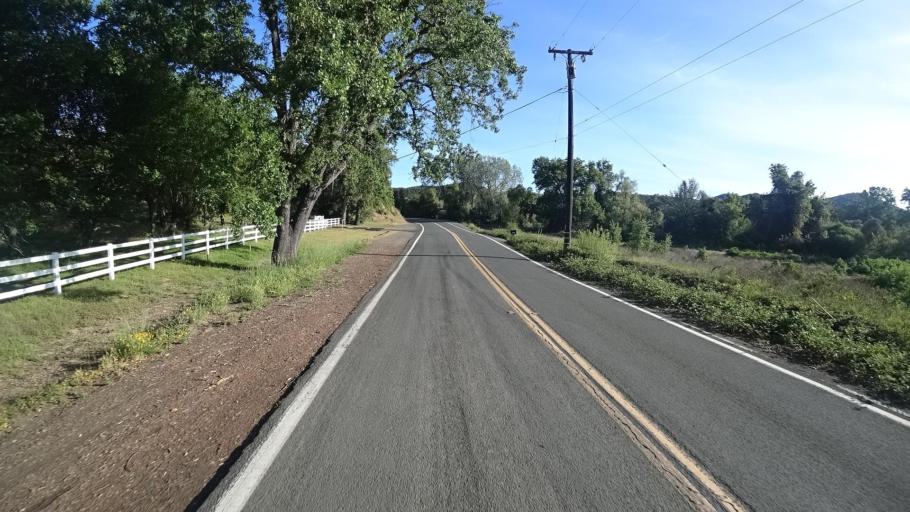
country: US
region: California
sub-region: Lake County
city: North Lakeport
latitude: 39.0903
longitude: -122.9497
